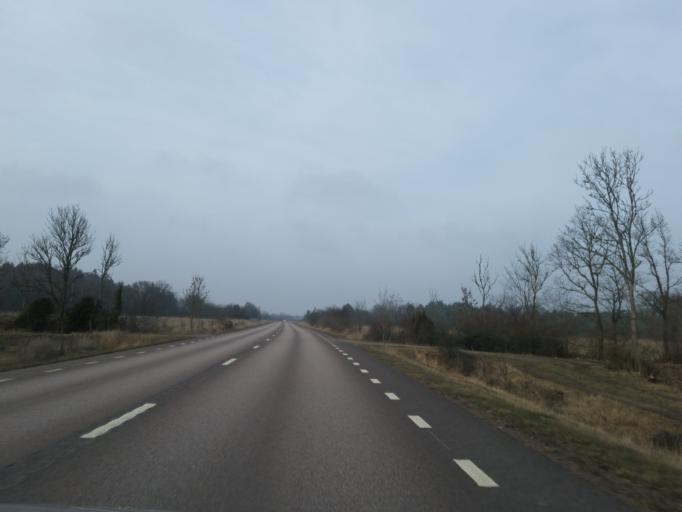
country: SE
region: Kalmar
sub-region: Borgholms Kommun
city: Borgholm
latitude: 57.0852
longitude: 16.9218
